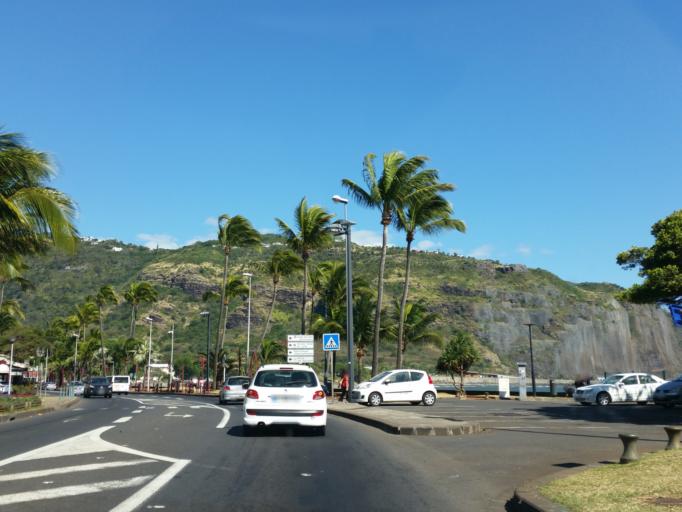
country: RE
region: Reunion
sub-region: Reunion
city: Saint-Denis
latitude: -20.8731
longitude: 55.4473
